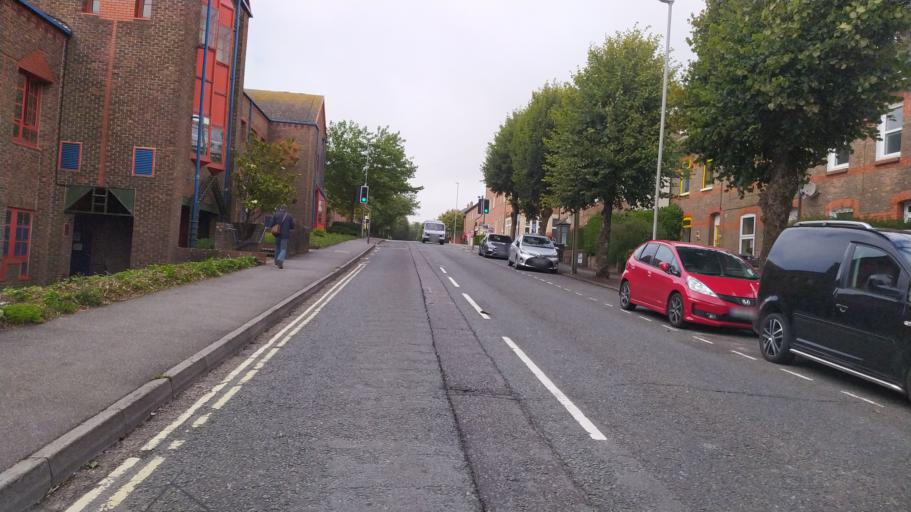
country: GB
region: England
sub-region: Dorset
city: Dorchester
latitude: 50.7139
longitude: -2.4467
